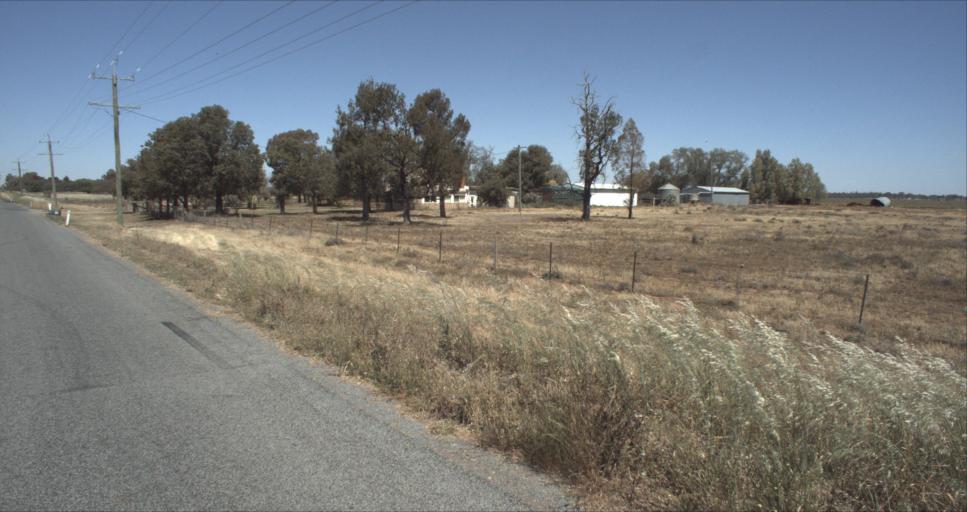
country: AU
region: New South Wales
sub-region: Leeton
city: Leeton
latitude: -34.5168
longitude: 146.4343
